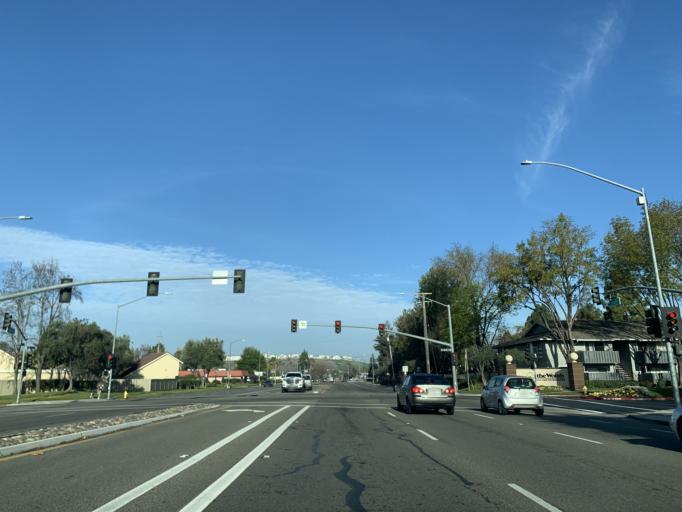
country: US
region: California
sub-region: Santa Clara County
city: Seven Trees
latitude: 37.2747
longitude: -121.8398
